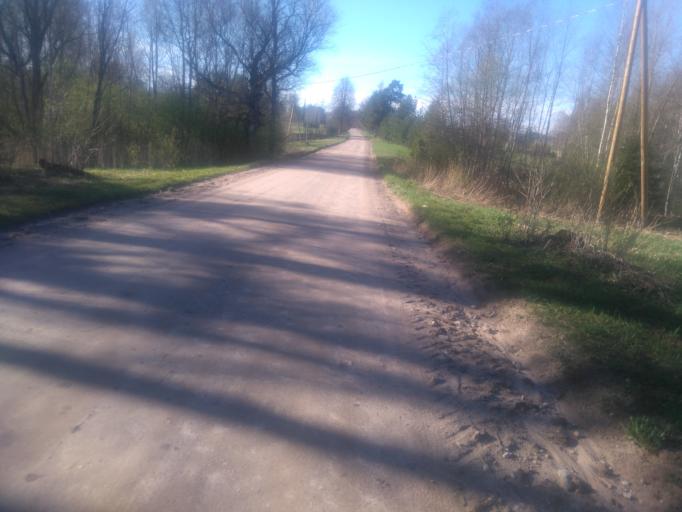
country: LV
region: Vecpiebalga
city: Vecpiebalga
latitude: 57.0146
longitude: 25.8367
